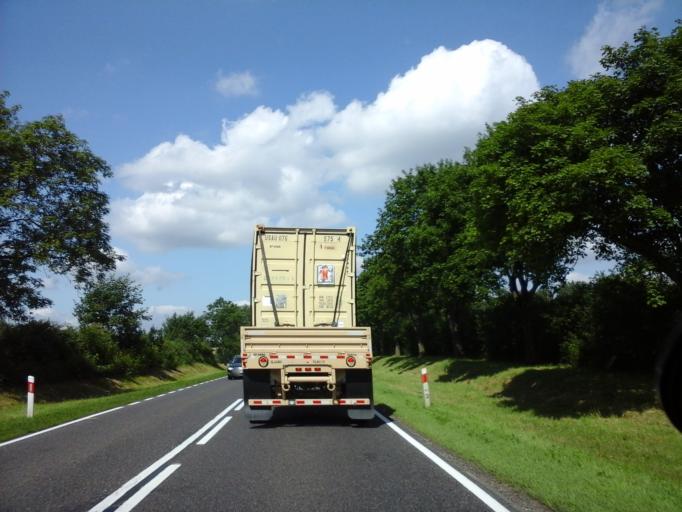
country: PL
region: West Pomeranian Voivodeship
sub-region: Powiat stargardzki
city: Stargard Szczecinski
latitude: 53.3080
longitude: 15.1333
